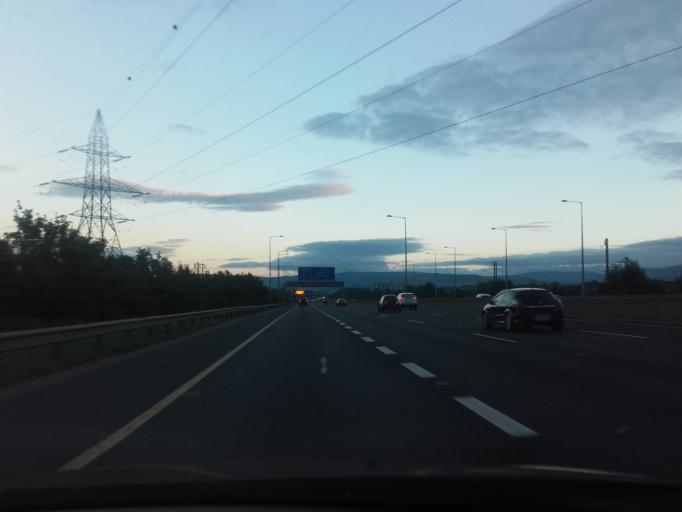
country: IE
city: Cherry Orchard
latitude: 53.3323
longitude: -6.3817
